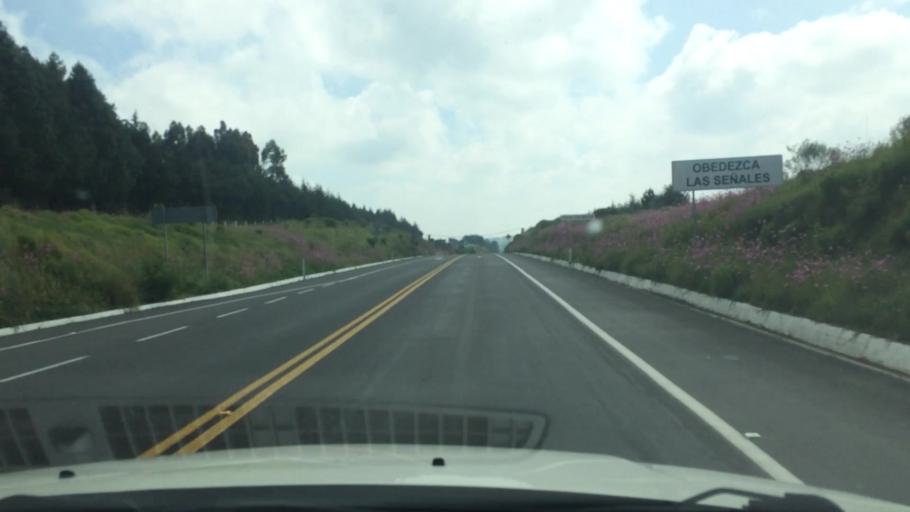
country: MX
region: Mexico
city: Amanalco de Becerra
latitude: 19.3547
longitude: -99.9815
